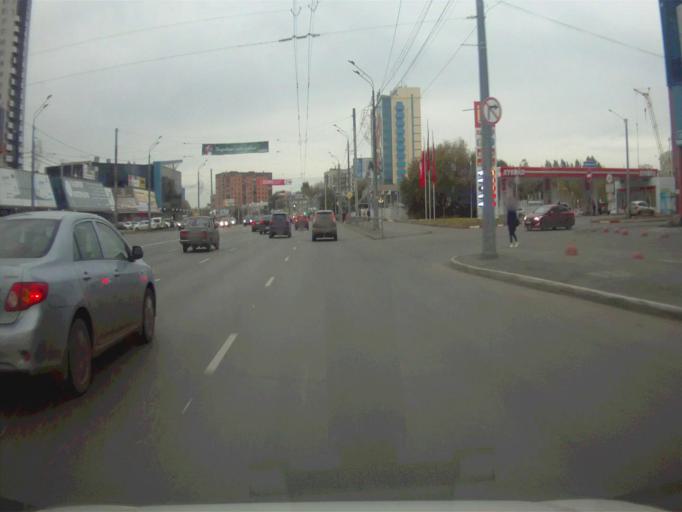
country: RU
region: Chelyabinsk
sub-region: Gorod Chelyabinsk
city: Chelyabinsk
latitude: 55.1690
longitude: 61.3757
